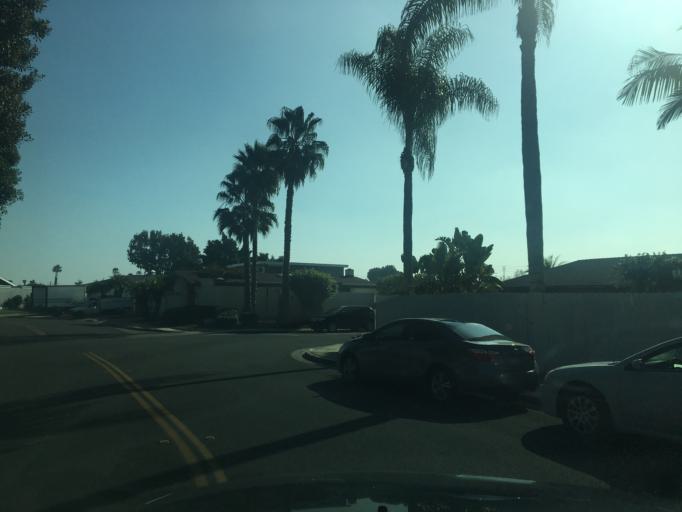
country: US
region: California
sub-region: Orange County
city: Tustin
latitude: 33.7320
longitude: -117.8228
